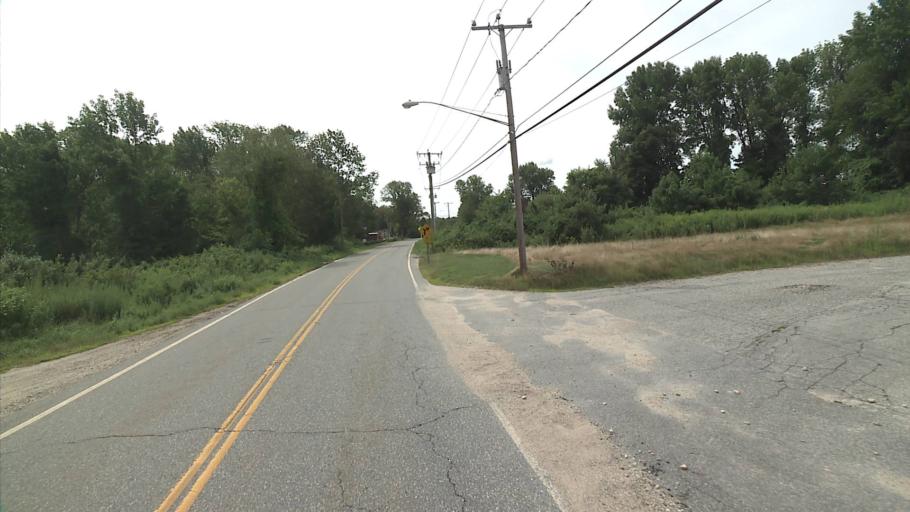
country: US
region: Connecticut
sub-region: Windham County
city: Thompson
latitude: 41.9775
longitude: -71.8448
